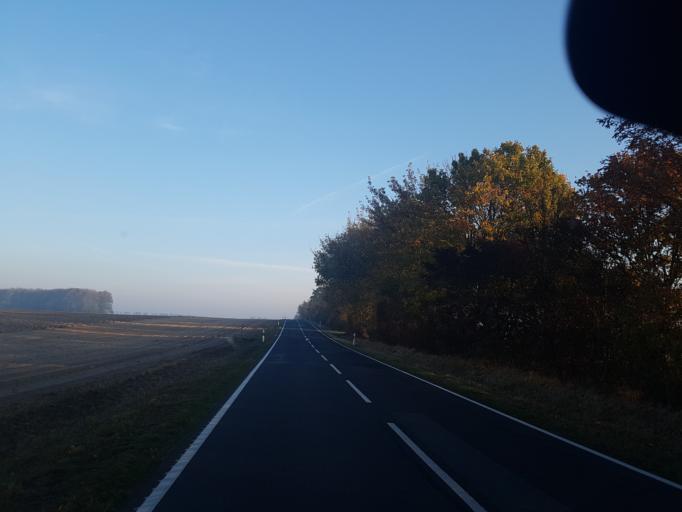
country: DE
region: Brandenburg
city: Juterbog
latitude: 51.9290
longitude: 13.0878
